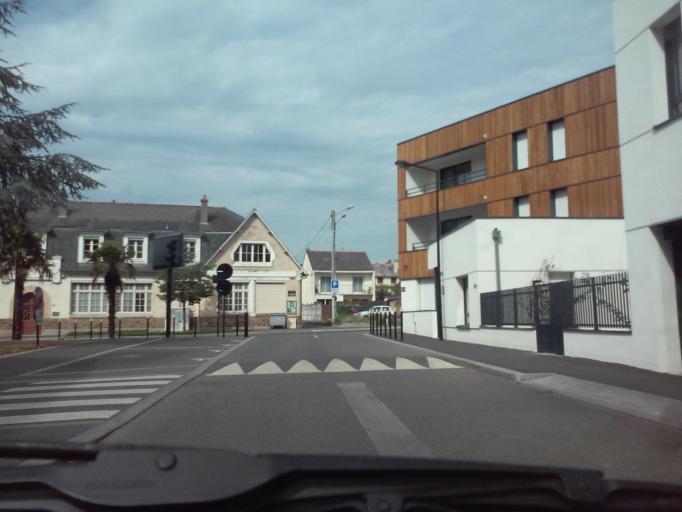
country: FR
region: Brittany
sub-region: Departement d'Ille-et-Vilaine
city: Rennes
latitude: 48.0902
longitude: -1.6951
